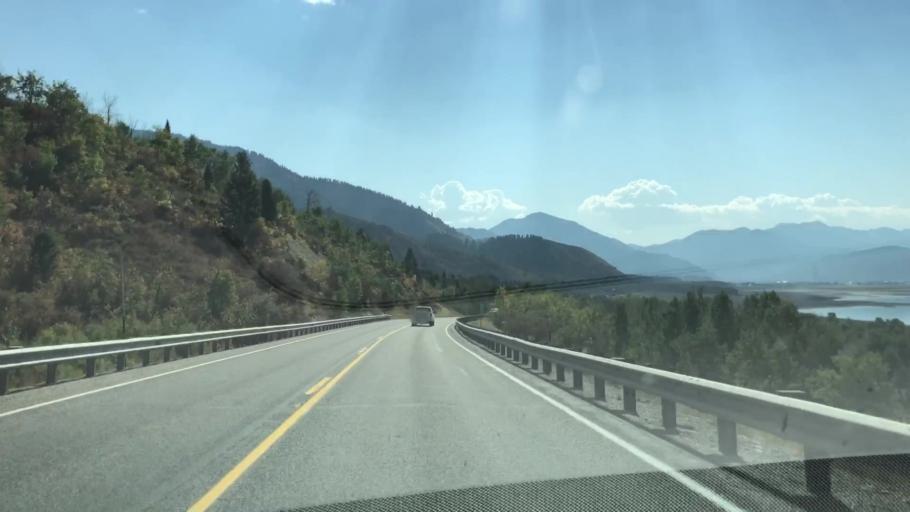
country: US
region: Wyoming
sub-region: Teton County
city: Hoback
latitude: 43.2255
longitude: -111.0804
